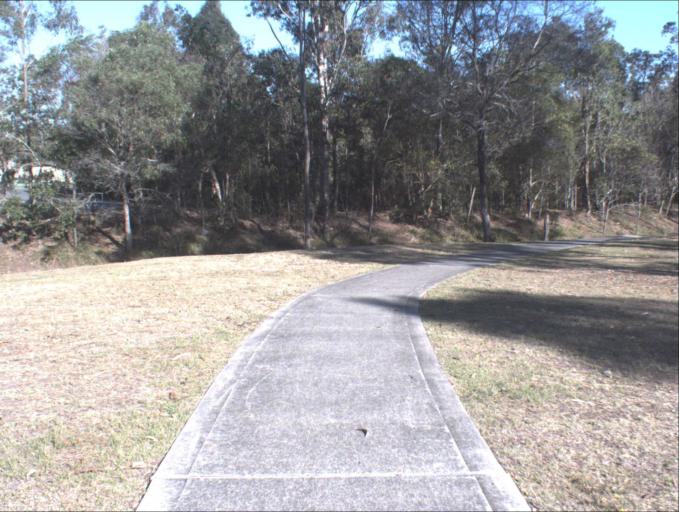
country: AU
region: Queensland
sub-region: Gold Coast
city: Yatala
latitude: -27.7046
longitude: 153.2224
